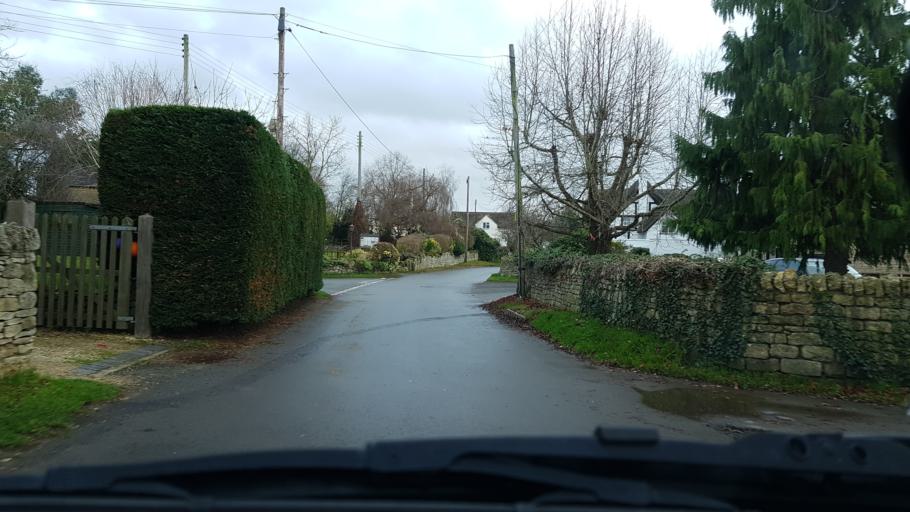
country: GB
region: England
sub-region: Worcestershire
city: Bredon
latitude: 52.0492
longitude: -2.1032
